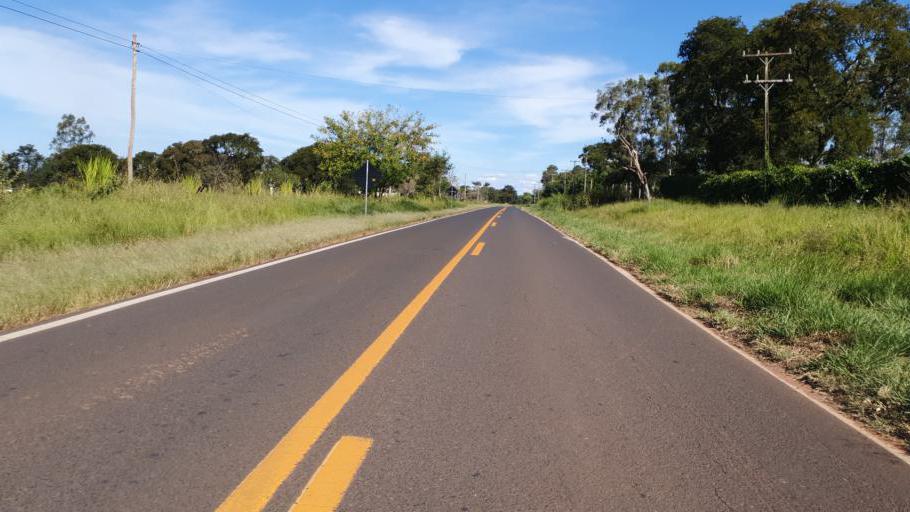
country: BR
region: Sao Paulo
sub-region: Paraguacu Paulista
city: Paraguacu Paulista
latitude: -22.3999
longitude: -50.5729
